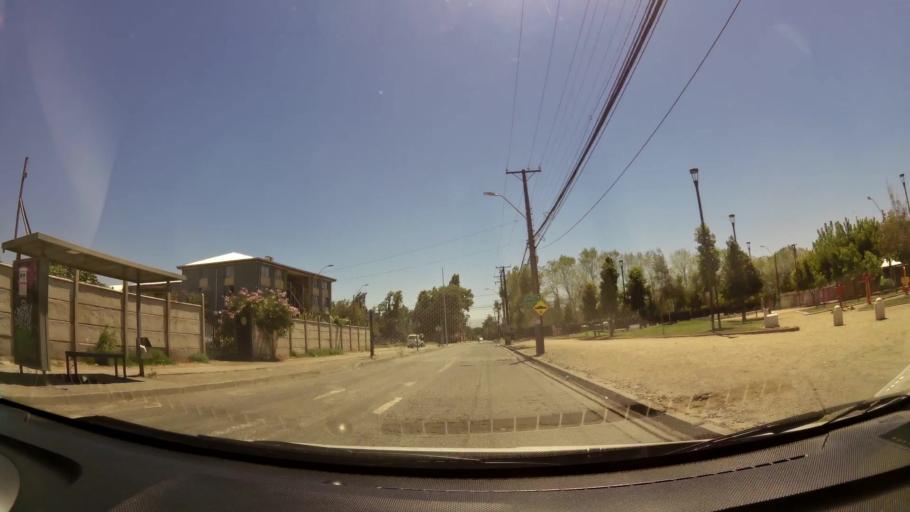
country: CL
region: O'Higgins
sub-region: Provincia de Cachapoal
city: Rancagua
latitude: -34.1498
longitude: -70.7234
